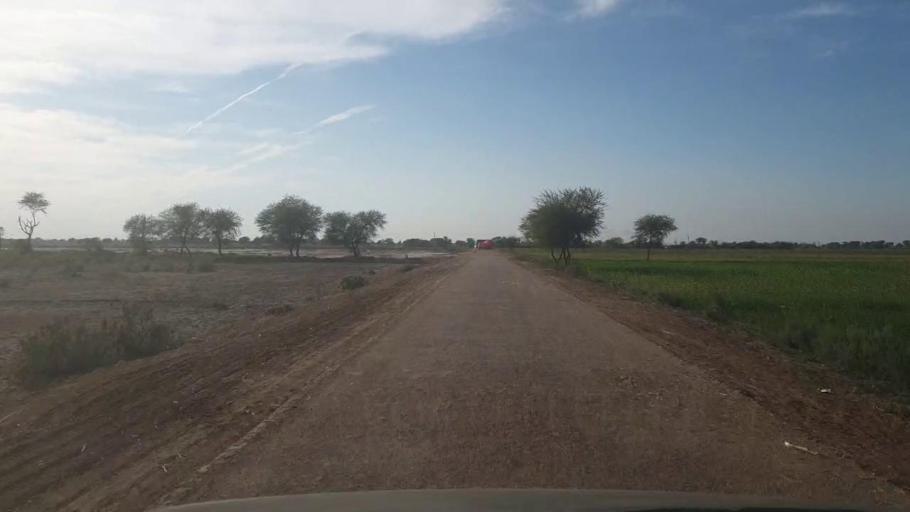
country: PK
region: Sindh
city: Samaro
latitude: 25.3320
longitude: 69.2433
